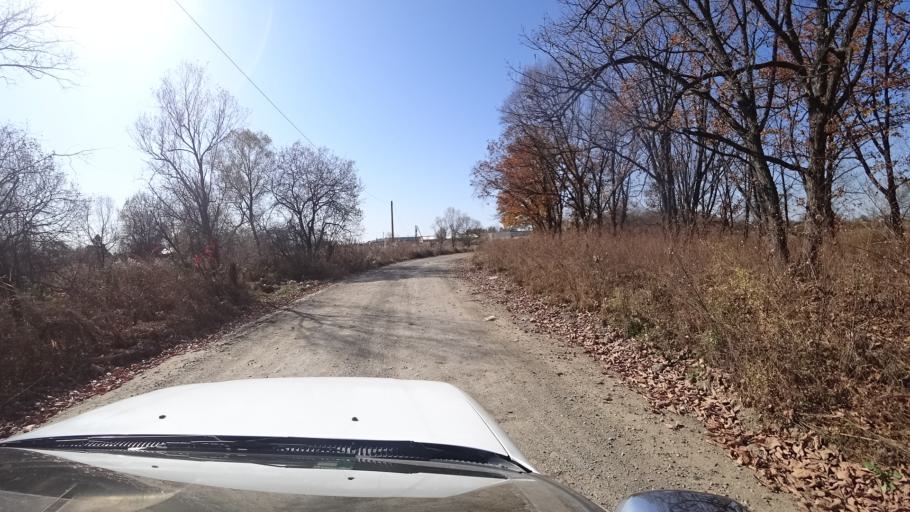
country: RU
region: Primorskiy
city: Dal'nerechensk
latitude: 45.9248
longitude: 133.7832
